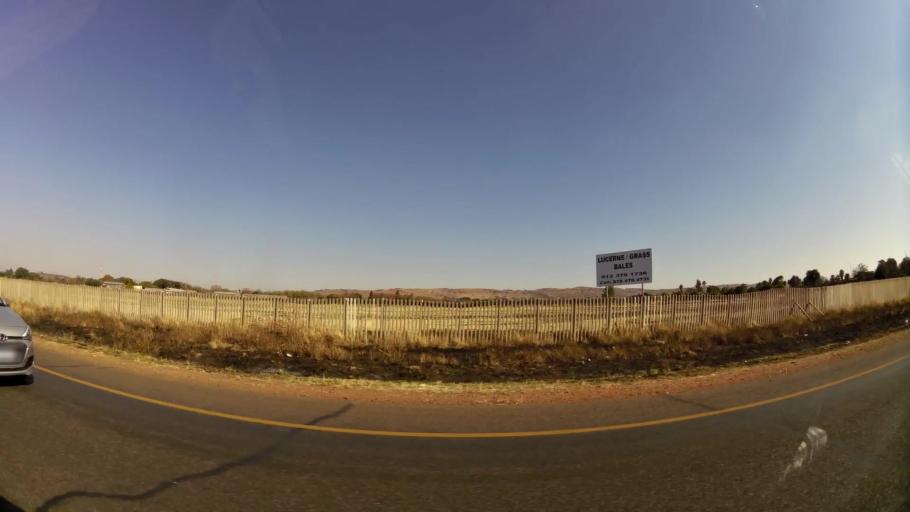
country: ZA
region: Gauteng
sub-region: City of Tshwane Metropolitan Municipality
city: Pretoria
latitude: -25.7056
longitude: 28.1608
